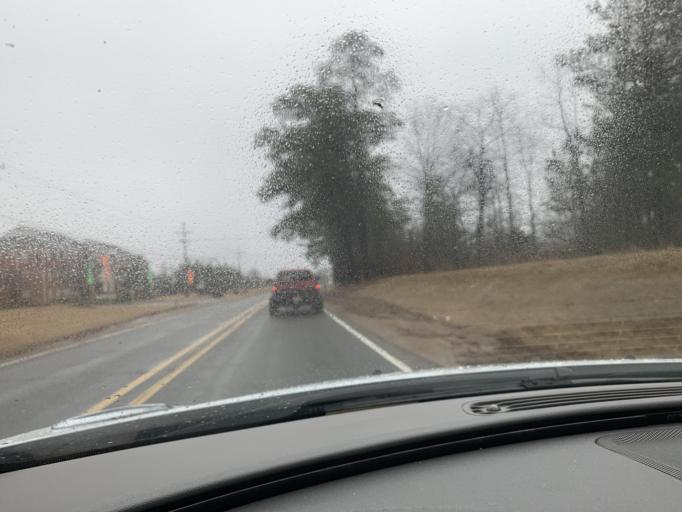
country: US
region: Mississippi
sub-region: De Soto County
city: Horn Lake
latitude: 34.9241
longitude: -90.0094
